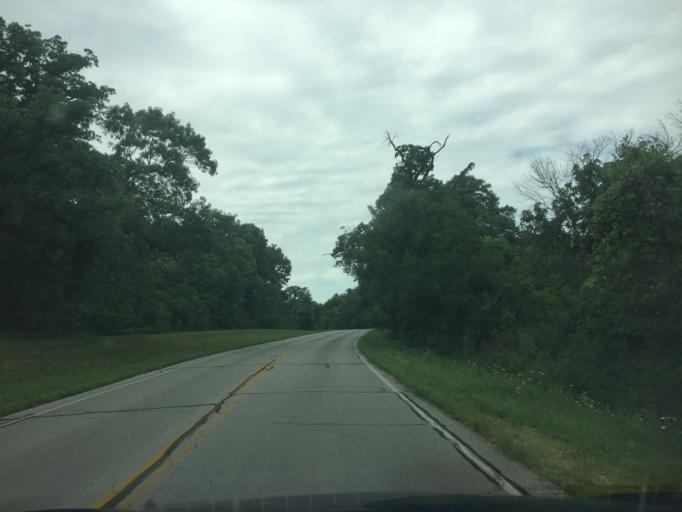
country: US
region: Missouri
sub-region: Platte County
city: Weston
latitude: 39.3715
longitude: -94.9340
